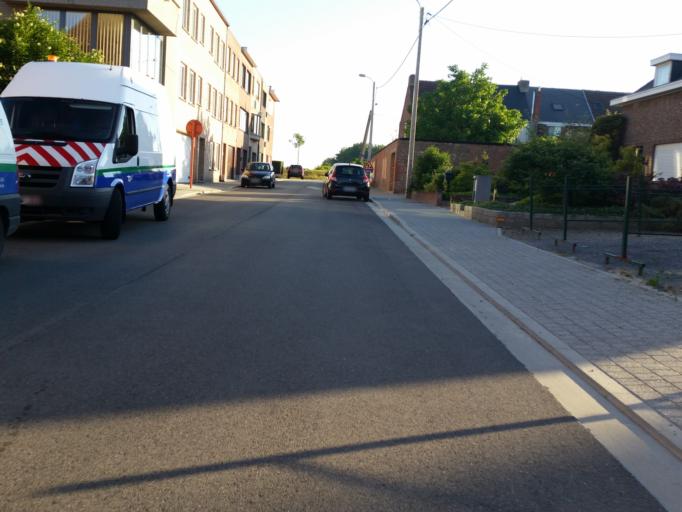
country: BE
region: Flanders
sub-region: Provincie Antwerpen
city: Mechelen
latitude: 51.0320
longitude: 4.4582
